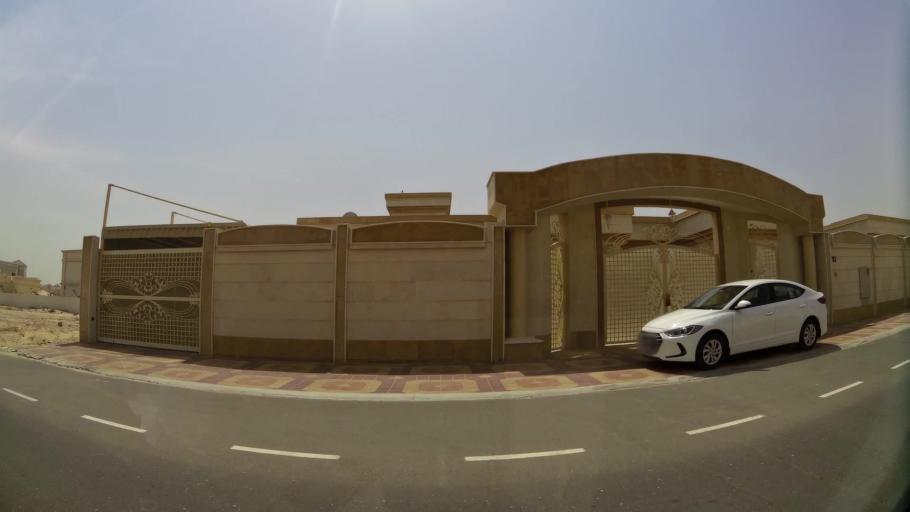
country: AE
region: Ash Shariqah
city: Sharjah
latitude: 25.2542
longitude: 55.4877
